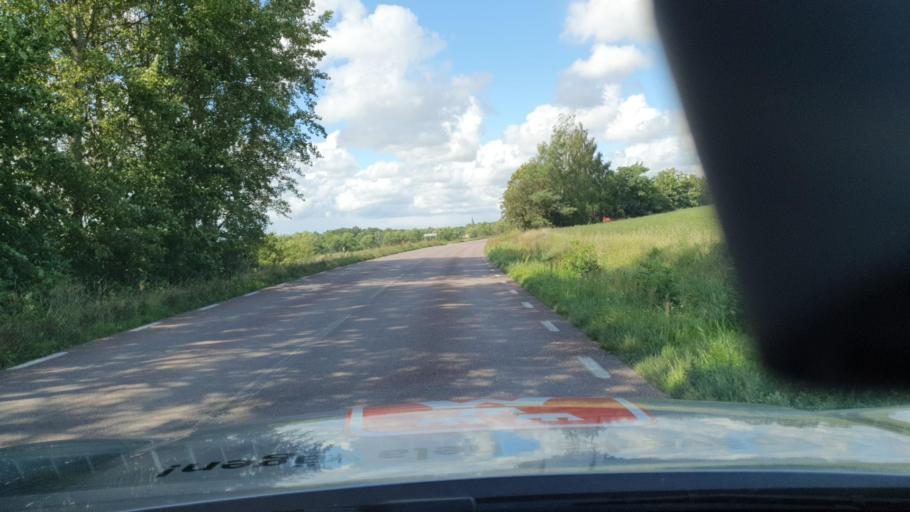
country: SE
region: Gotland
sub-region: Gotland
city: Hemse
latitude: 57.1526
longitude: 18.3376
